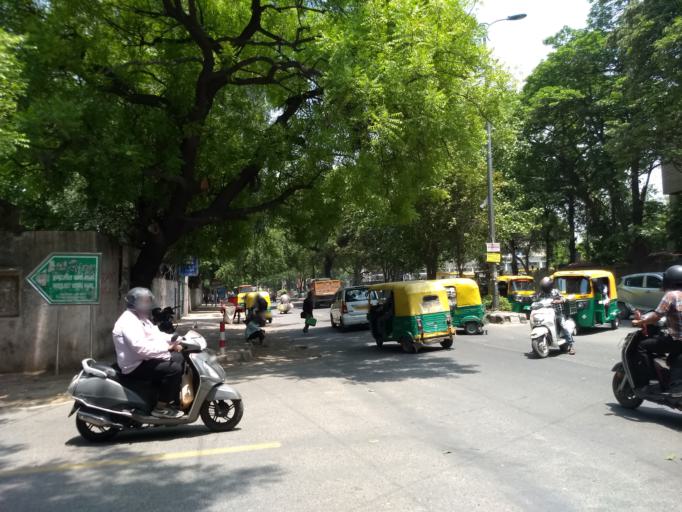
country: IN
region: NCT
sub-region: New Delhi
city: New Delhi
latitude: 28.5326
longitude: 77.2039
